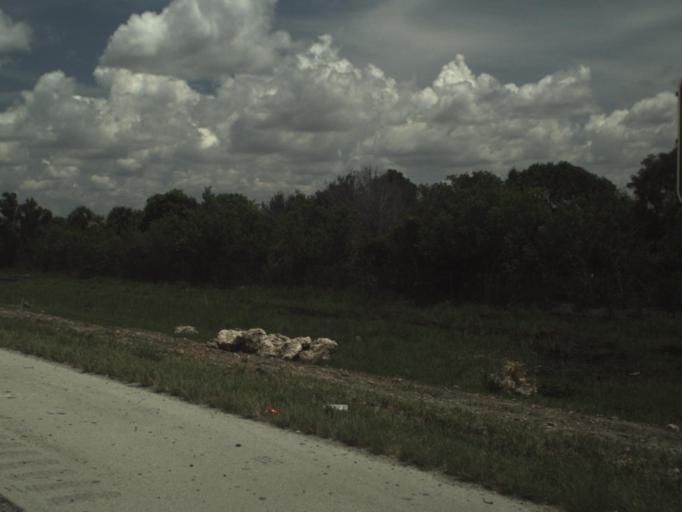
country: US
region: Florida
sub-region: Broward County
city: Sunshine Ranches
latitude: 26.0182
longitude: -80.3455
